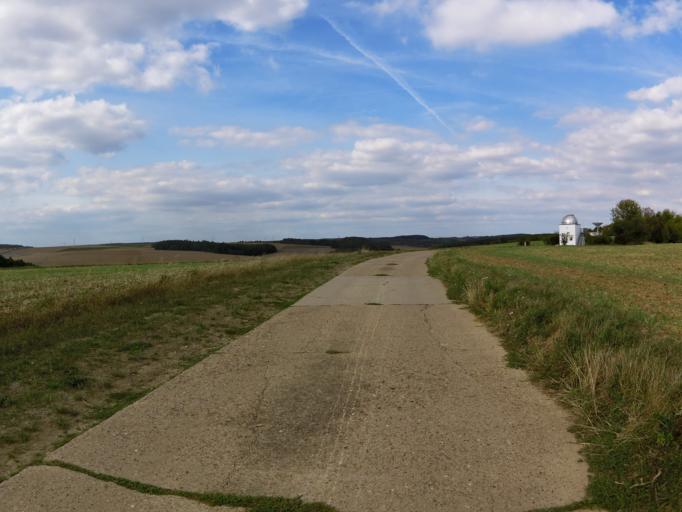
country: DE
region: Bavaria
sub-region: Regierungsbezirk Unterfranken
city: Hettstadt
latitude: 49.7929
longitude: 9.7956
